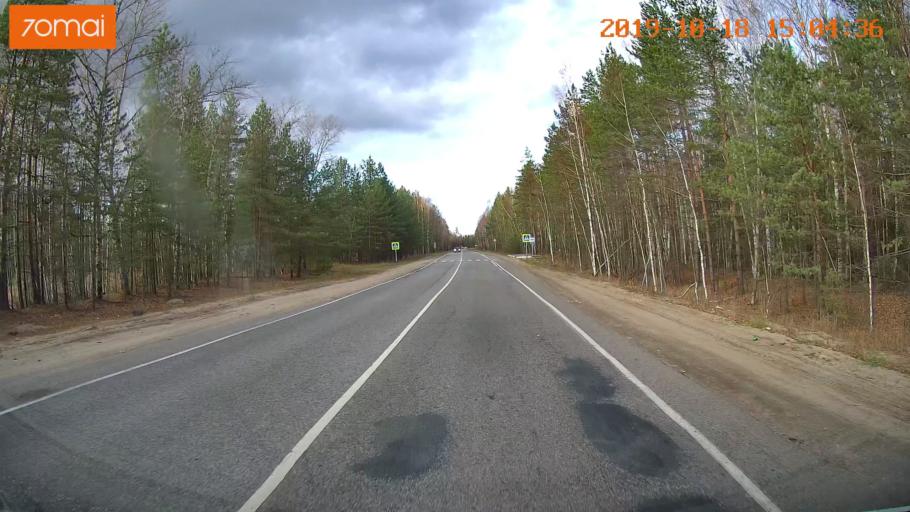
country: RU
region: Vladimir
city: Kurlovo
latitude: 55.5047
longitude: 40.5715
